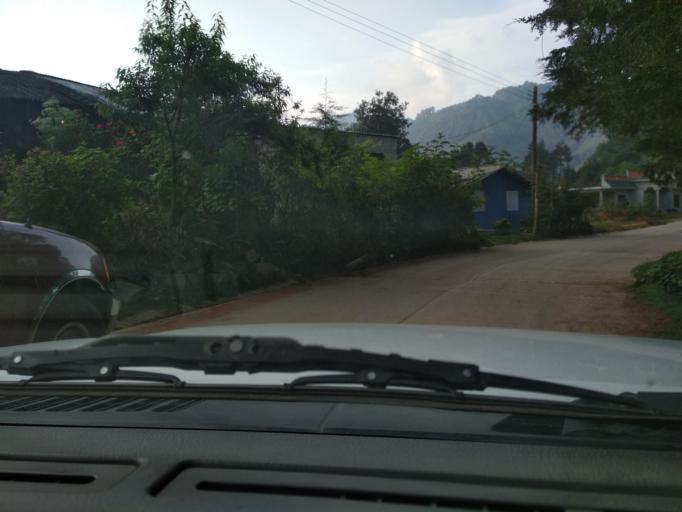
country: MX
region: Veracruz
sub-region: Soledad Atzompa
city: Tlatilpa
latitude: 18.7484
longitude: -97.1535
